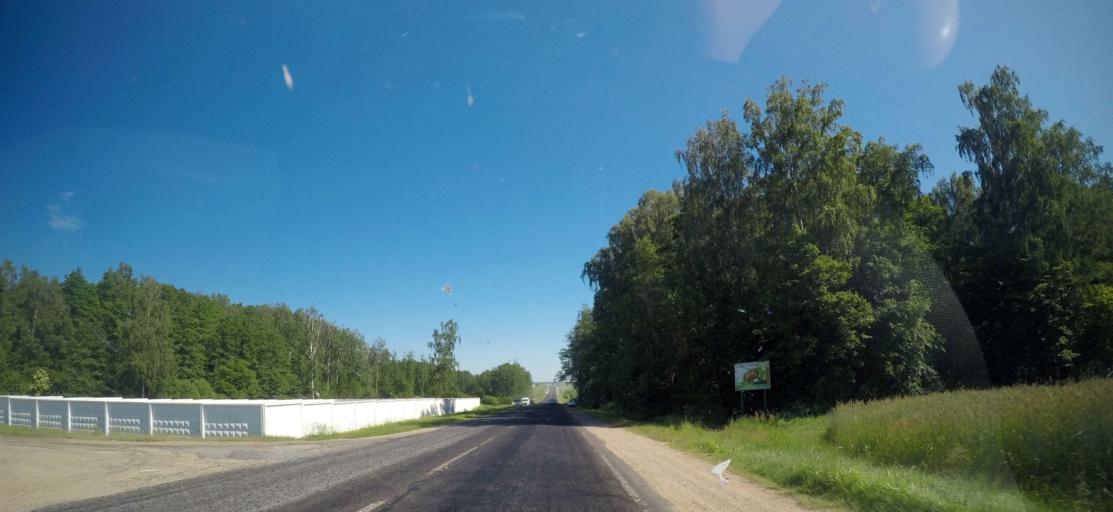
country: BY
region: Grodnenskaya
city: Vyalikaya Byerastavitsa
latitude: 53.2195
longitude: 23.9972
